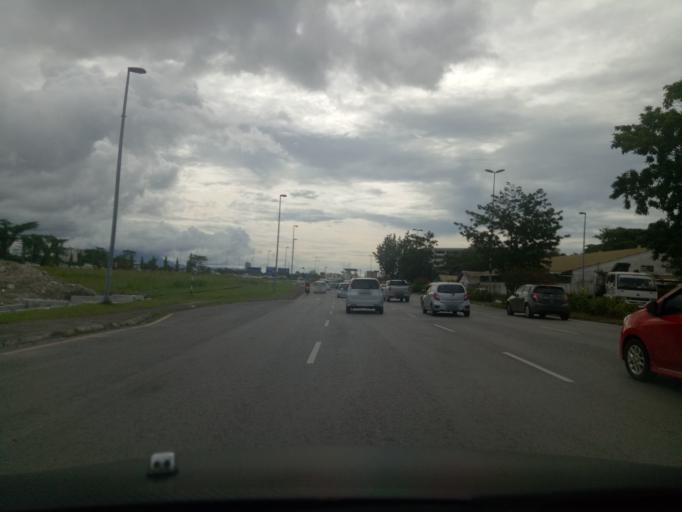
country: MY
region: Sarawak
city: Kuching
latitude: 1.5549
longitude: 110.3838
